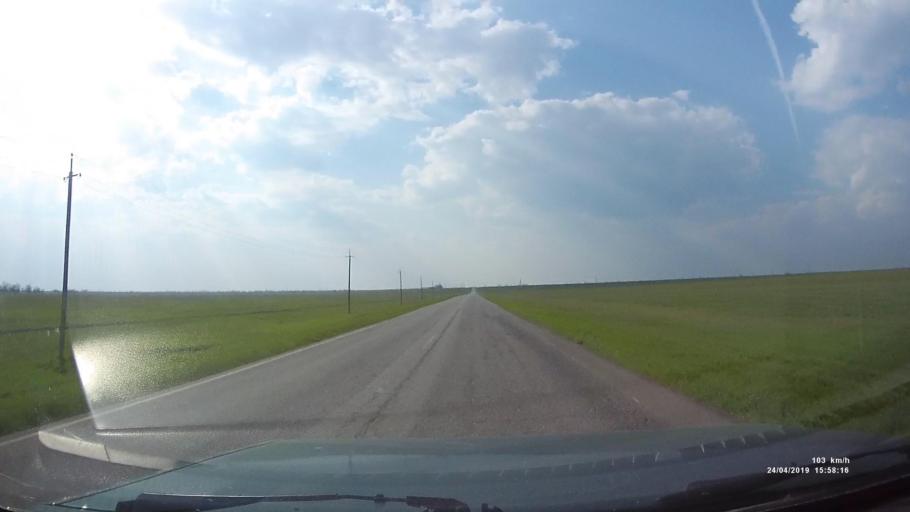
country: RU
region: Kalmykiya
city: Yashalta
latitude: 46.6125
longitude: 42.4934
